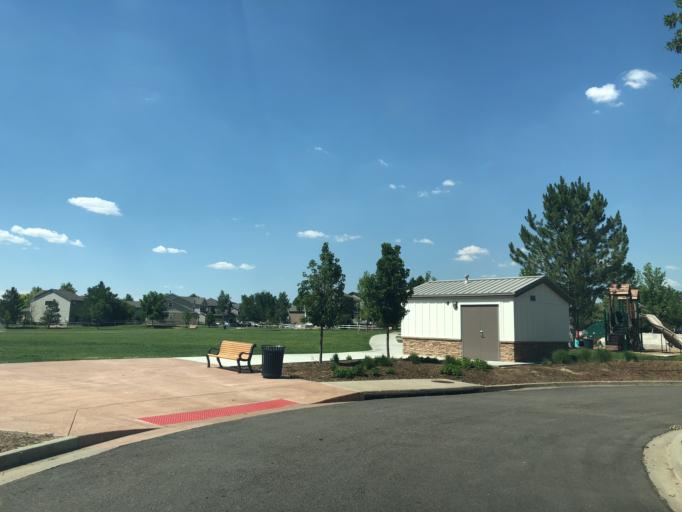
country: US
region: Colorado
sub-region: Arapahoe County
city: Dove Valley
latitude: 39.6052
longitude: -104.7759
